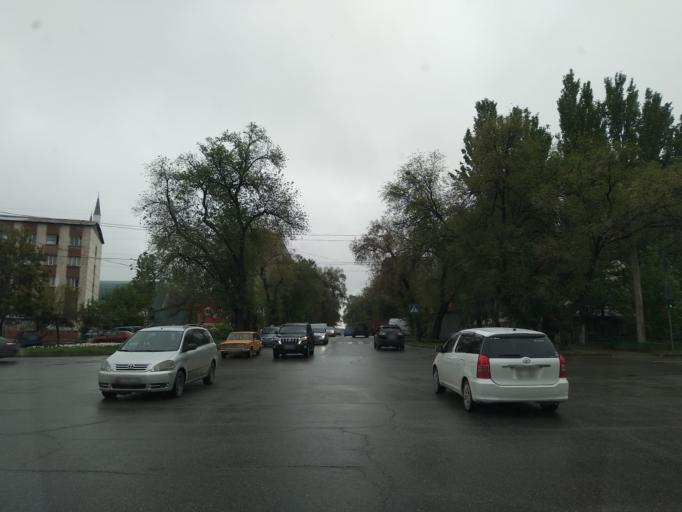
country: KG
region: Chuy
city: Bishkek
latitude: 42.8825
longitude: 74.6172
